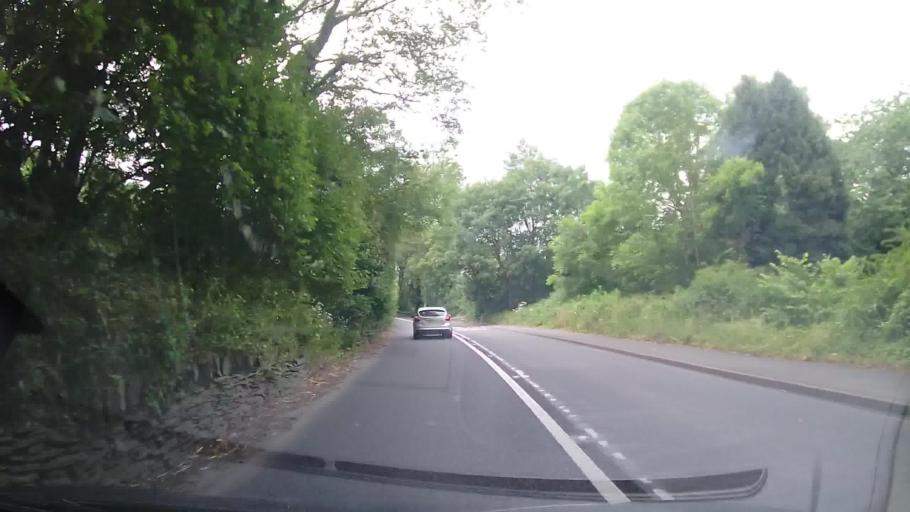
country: GB
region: Wales
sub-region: Denbighshire
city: Corwen
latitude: 52.9804
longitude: -3.3407
